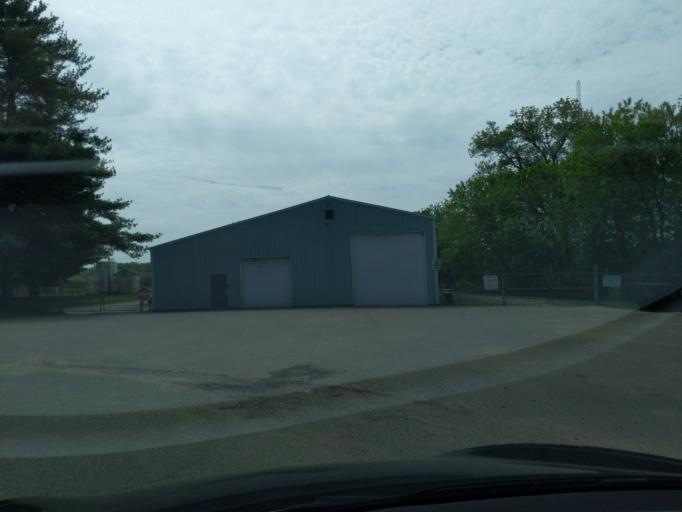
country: US
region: Michigan
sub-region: Ingham County
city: Stockbridge
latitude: 42.4469
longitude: -84.1752
